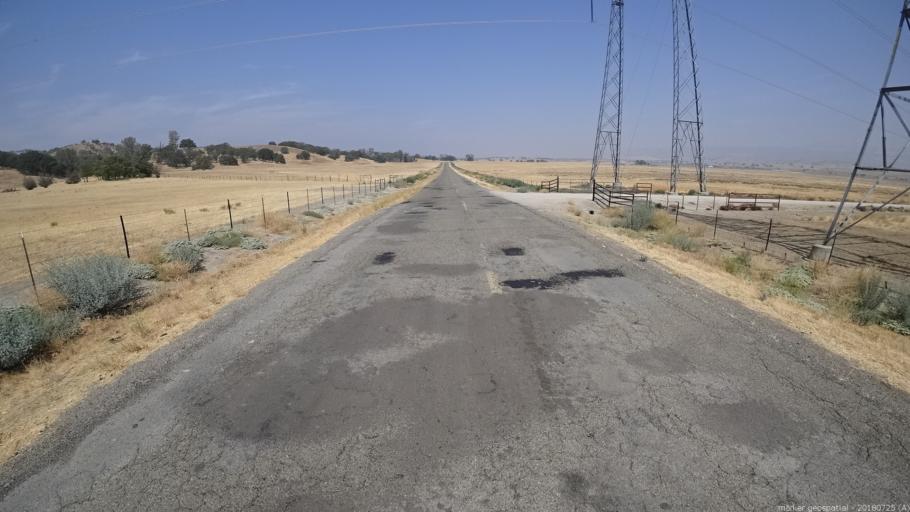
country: US
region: California
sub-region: San Luis Obispo County
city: Shandon
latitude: 35.8183
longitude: -120.3796
